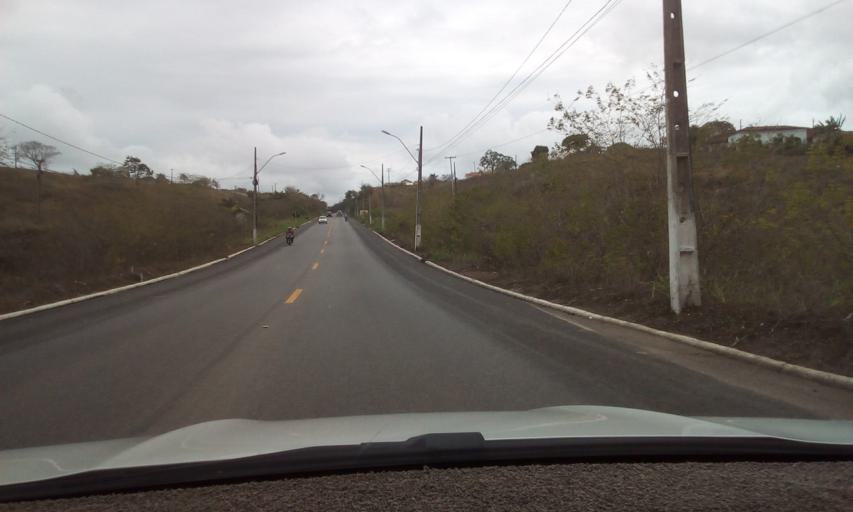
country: BR
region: Paraiba
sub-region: Lagoa Seca
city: Lagoa Seca
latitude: -7.1940
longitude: -35.8722
